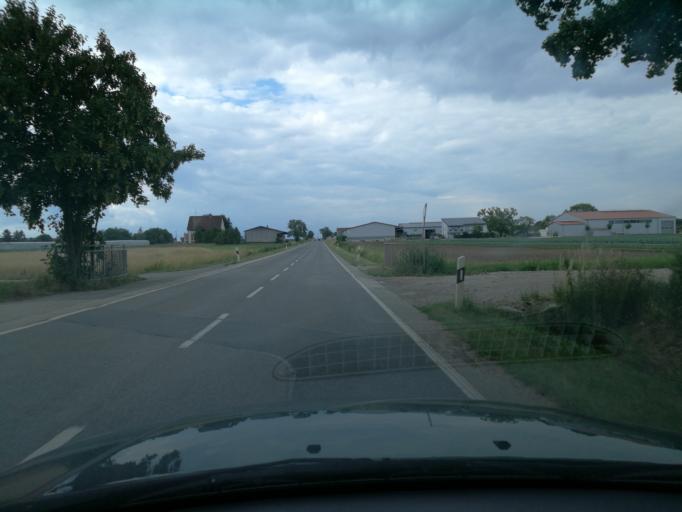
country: DE
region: Bavaria
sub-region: Regierungsbezirk Mittelfranken
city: Wetzendorf
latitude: 49.4853
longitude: 11.0366
